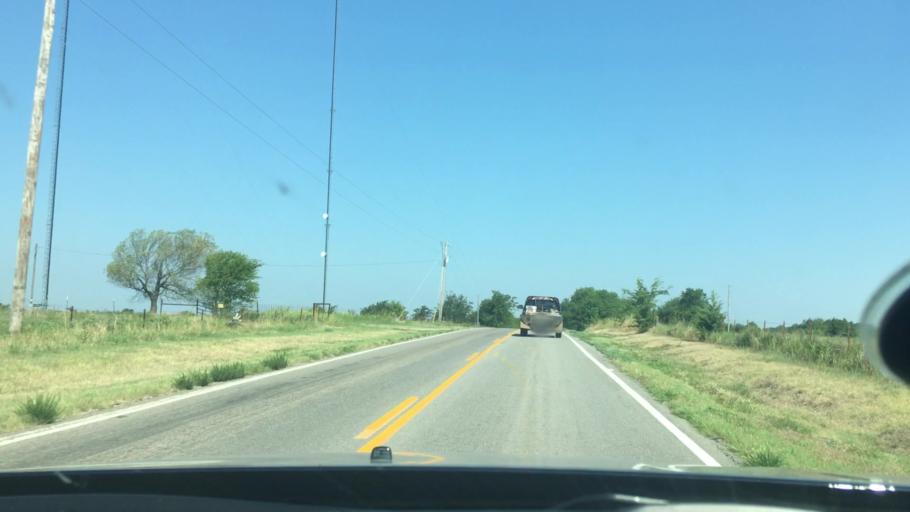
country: US
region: Oklahoma
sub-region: Johnston County
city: Tishomingo
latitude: 34.1931
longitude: -96.5346
